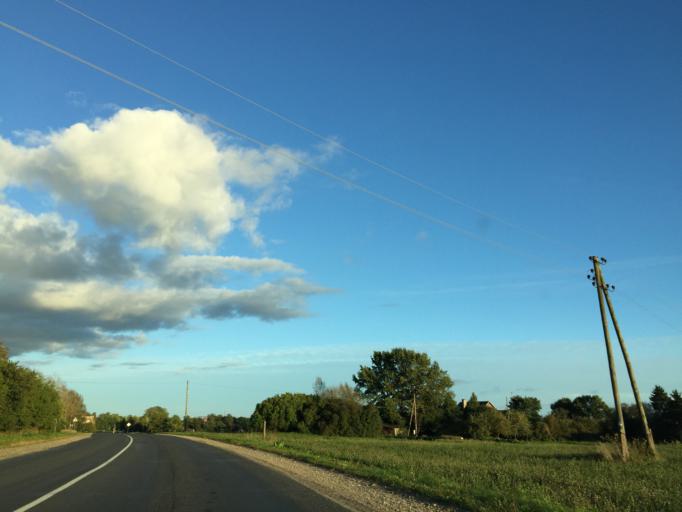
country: LV
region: Saldus Rajons
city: Saldus
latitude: 56.6957
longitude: 22.4369
